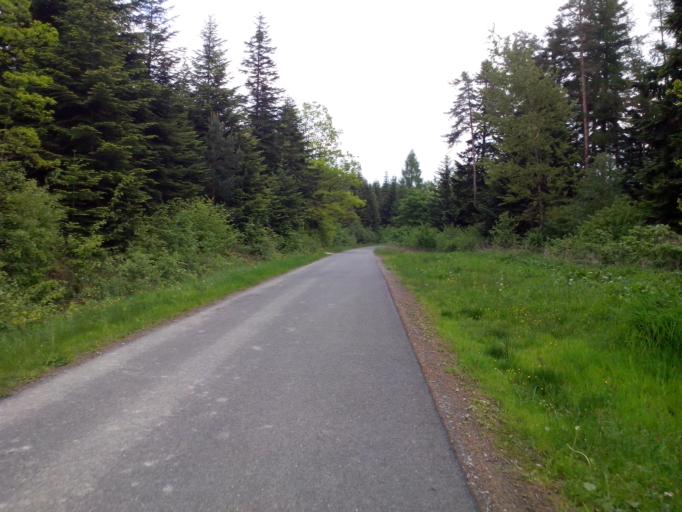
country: PL
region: Subcarpathian Voivodeship
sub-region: Powiat strzyzowski
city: Wysoka Strzyzowska
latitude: 49.8206
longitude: 21.7869
